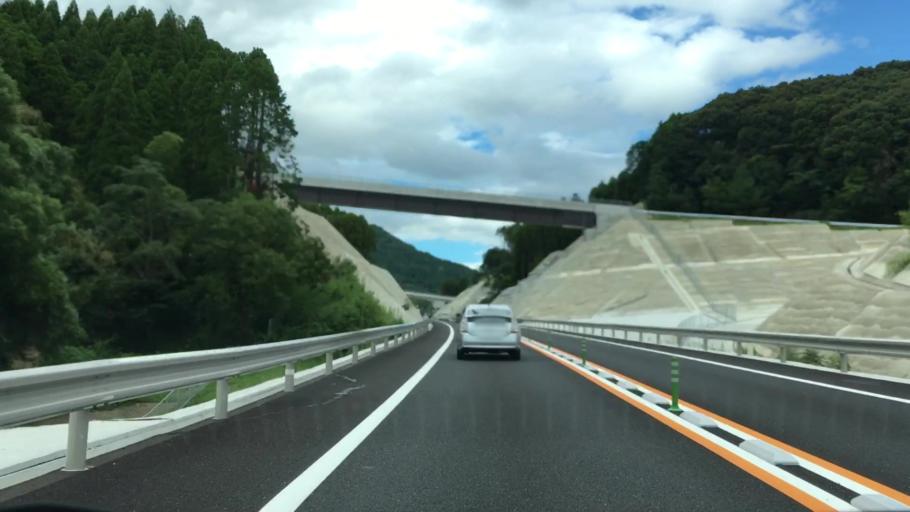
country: JP
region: Saga Prefecture
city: Imaricho-ko
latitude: 33.3028
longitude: 129.9157
